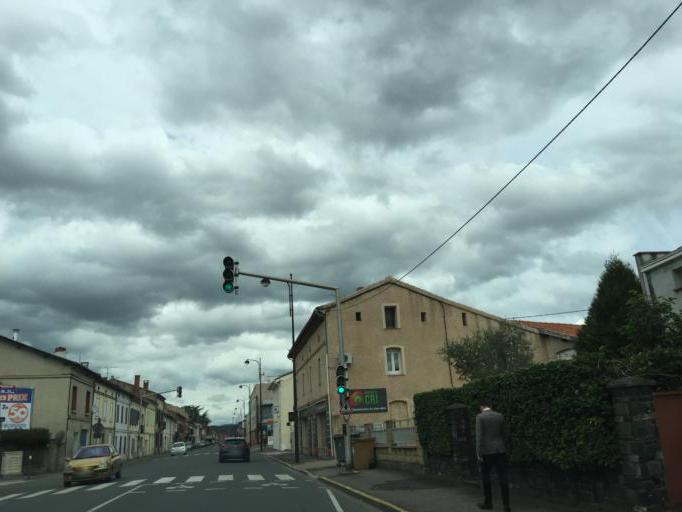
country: FR
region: Midi-Pyrenees
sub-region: Departement du Tarn
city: Albi
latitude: 43.9391
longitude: 2.1480
